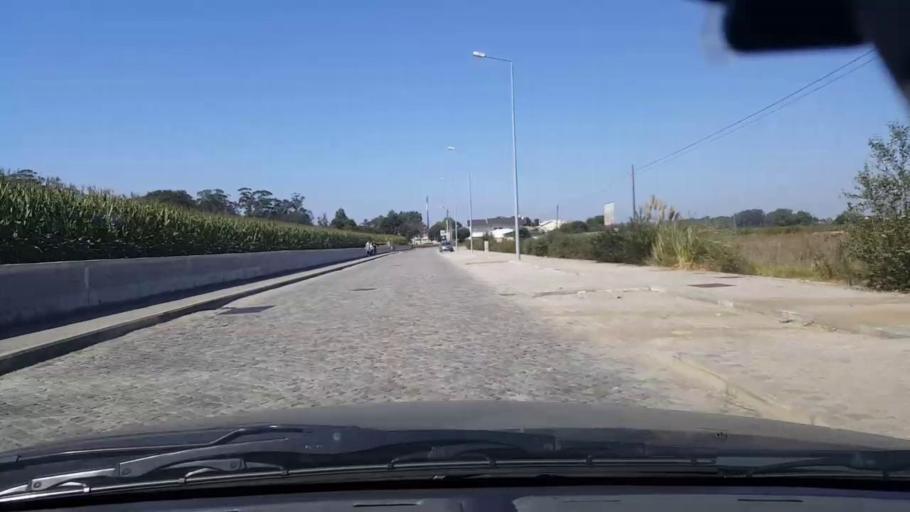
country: PT
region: Porto
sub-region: Vila do Conde
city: Arvore
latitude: 41.3059
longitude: -8.7166
